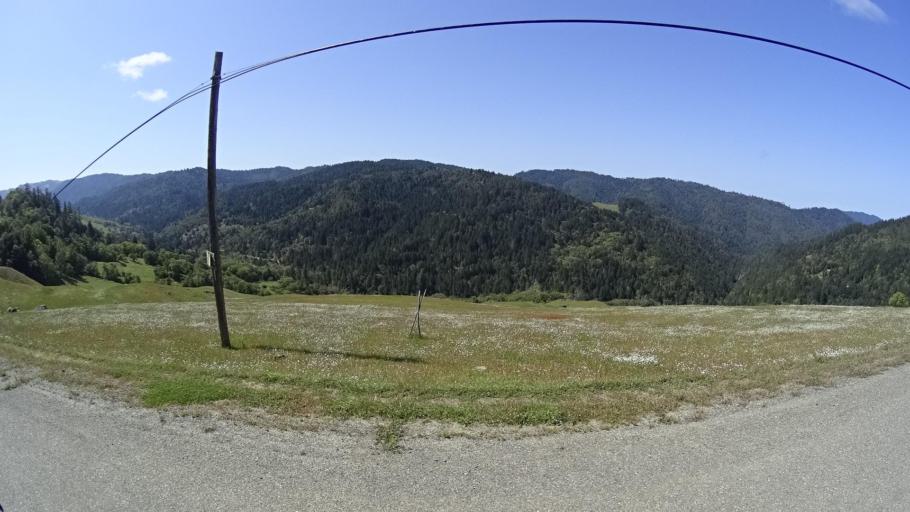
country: US
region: California
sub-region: Humboldt County
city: Redway
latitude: 40.0240
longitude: -123.6297
